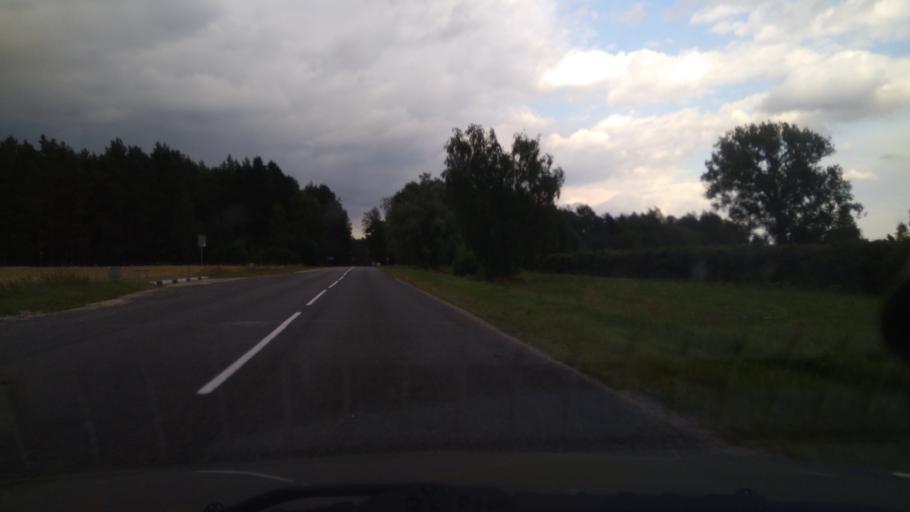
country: BY
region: Minsk
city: Il'ya
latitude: 54.4305
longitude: 27.2145
